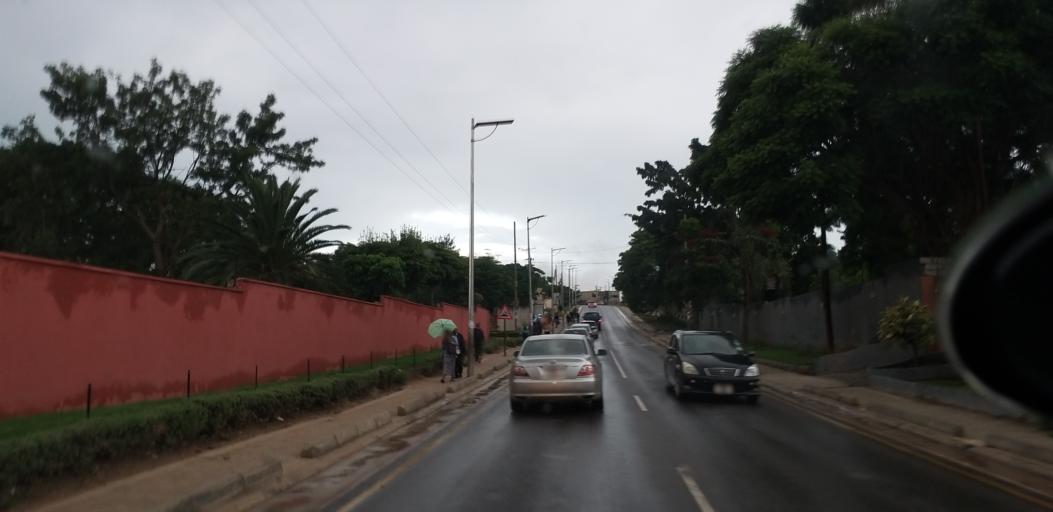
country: ZM
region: Lusaka
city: Lusaka
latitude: -15.4167
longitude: 28.3608
